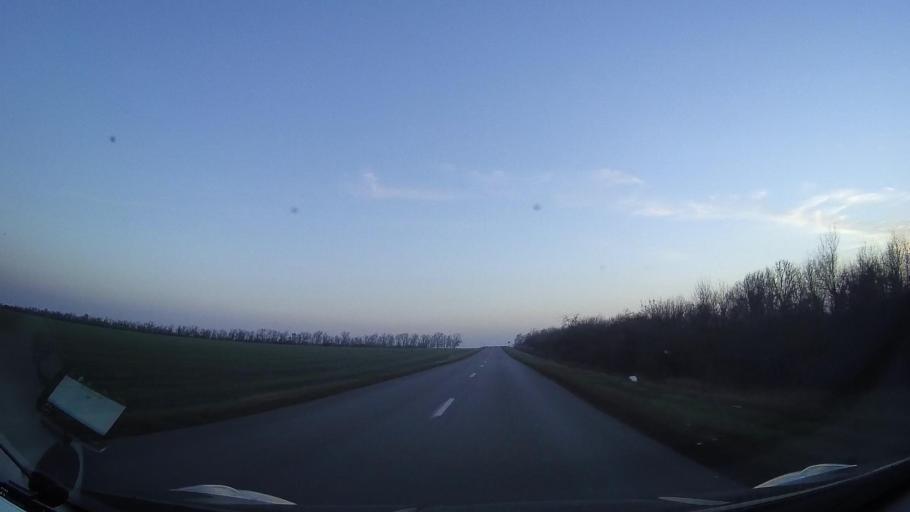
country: RU
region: Rostov
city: Zernograd
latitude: 46.9155
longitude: 40.3388
